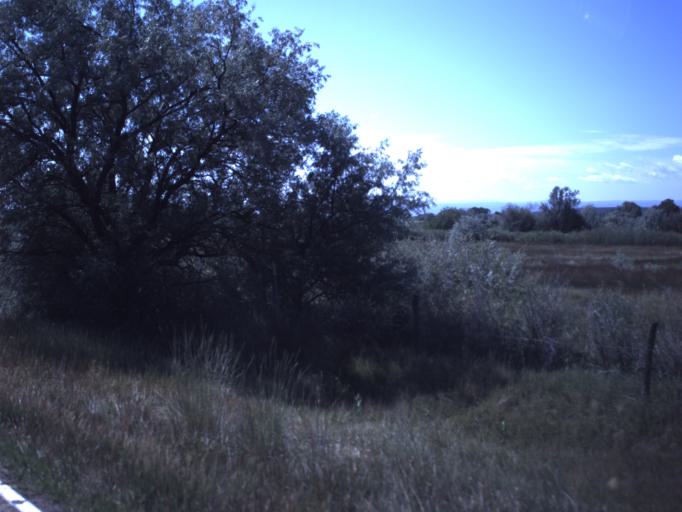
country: US
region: Utah
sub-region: Duchesne County
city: Duchesne
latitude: 40.3251
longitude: -110.2640
